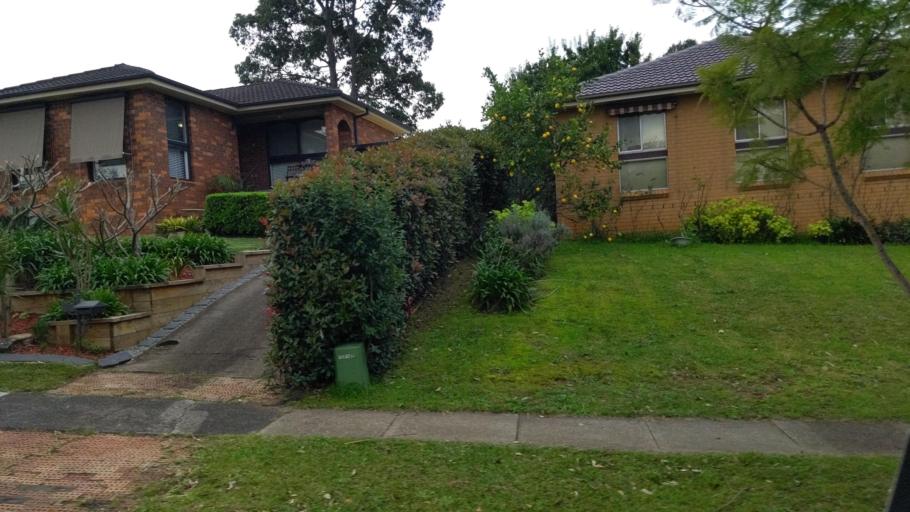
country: AU
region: New South Wales
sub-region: Blacktown
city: Blacktown
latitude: -33.7522
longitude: 150.9371
